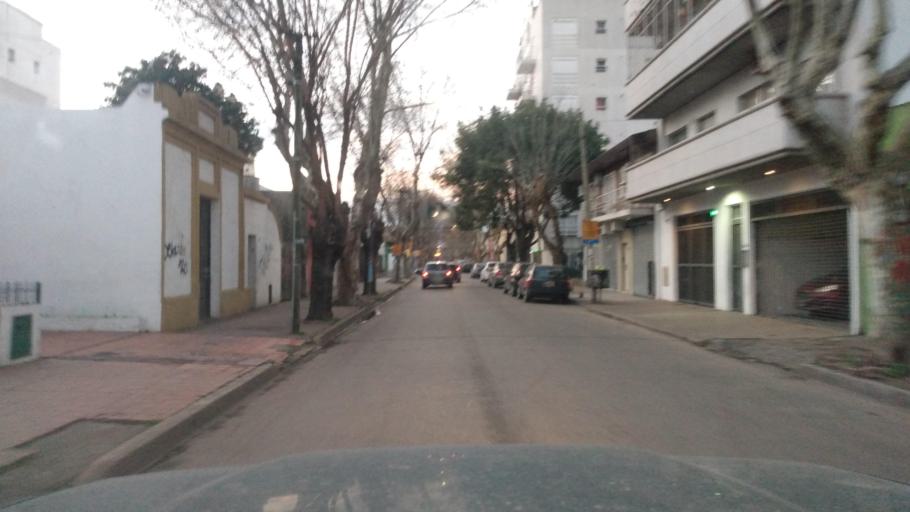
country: AR
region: Buenos Aires
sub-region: Partido de Pilar
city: Pilar
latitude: -34.4624
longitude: -58.9144
